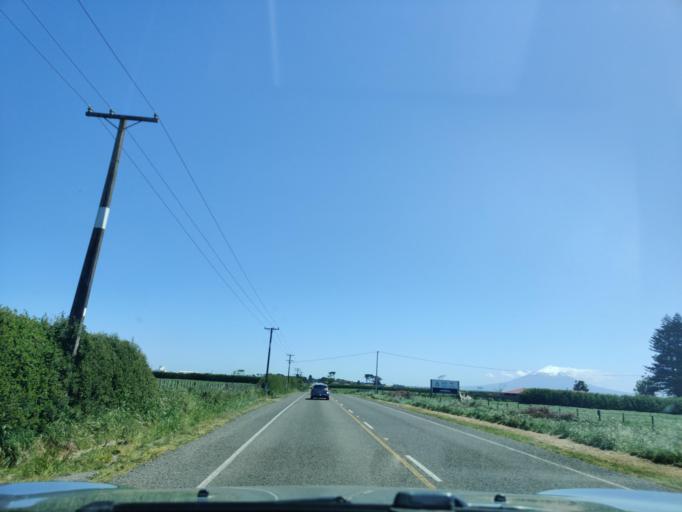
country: NZ
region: Taranaki
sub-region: South Taranaki District
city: Hawera
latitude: -39.6133
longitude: 174.3307
